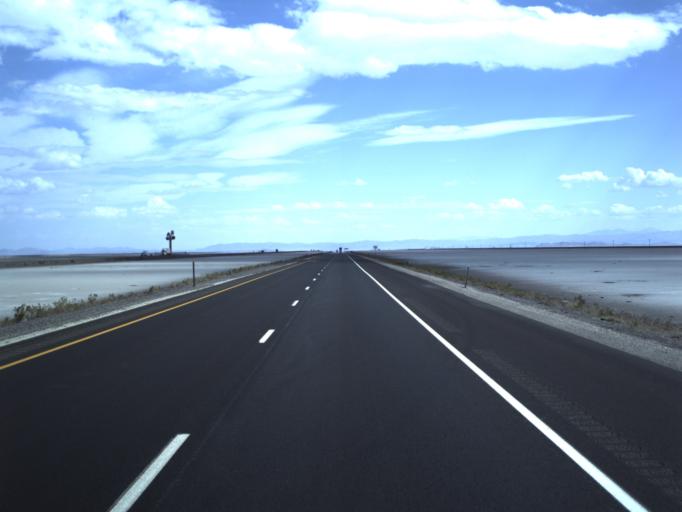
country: US
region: Utah
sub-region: Tooele County
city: Wendover
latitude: 40.7323
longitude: -113.5622
